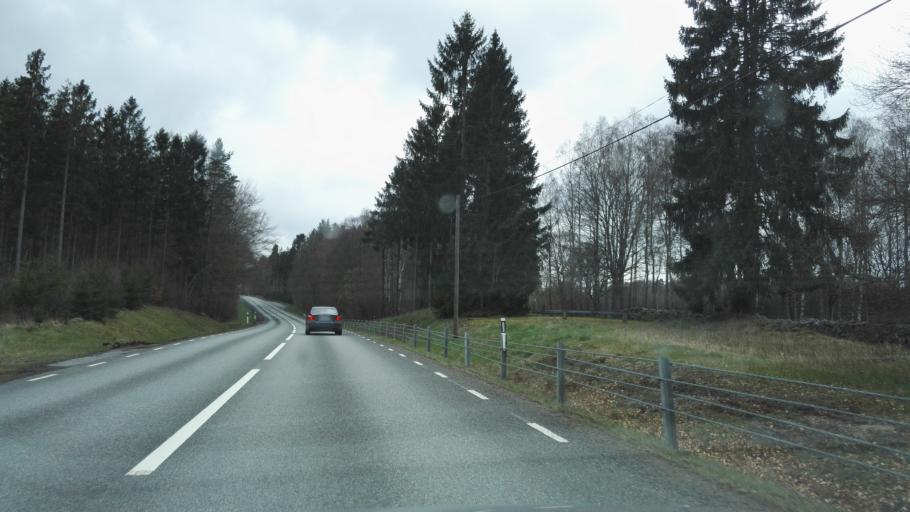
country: SE
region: Skane
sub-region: Hassleholms Kommun
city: Hastveda
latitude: 56.2204
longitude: 13.9678
